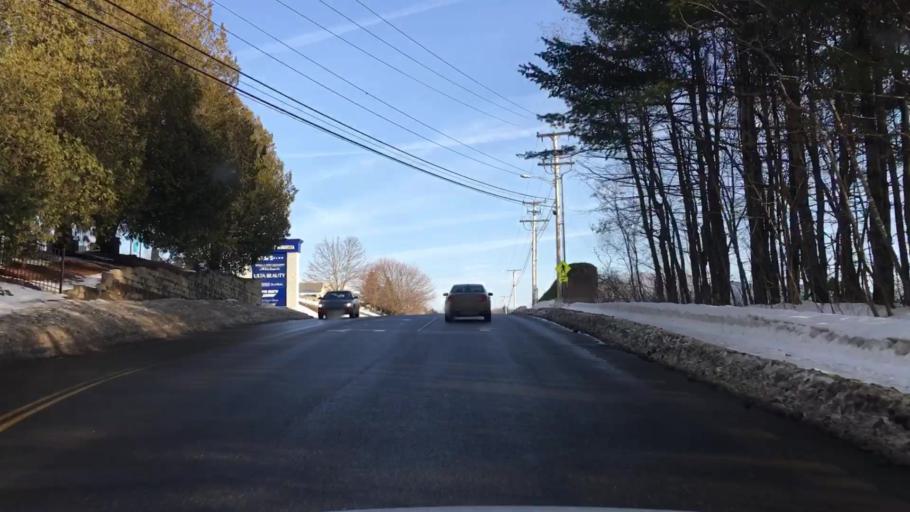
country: US
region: Maine
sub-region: Kennebec County
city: Augusta
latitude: 44.3397
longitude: -69.7907
